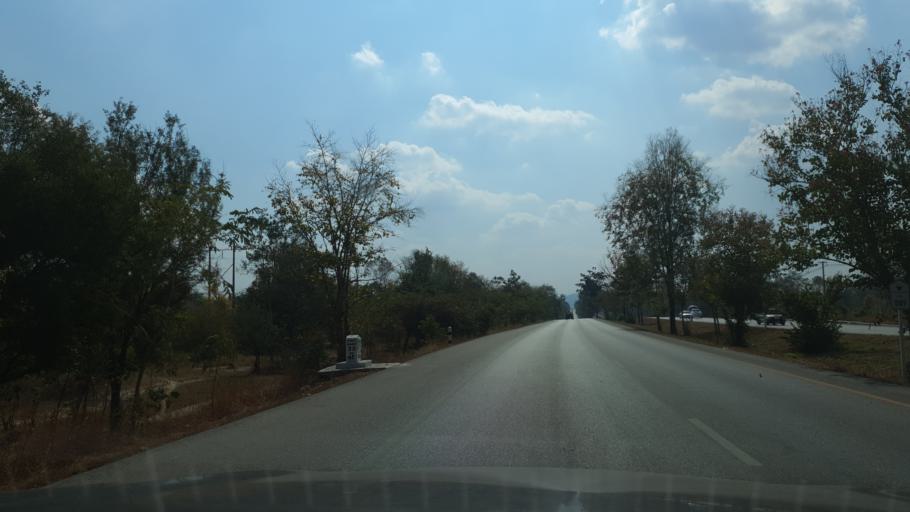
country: TH
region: Lampang
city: Mae Phrik
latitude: 17.3992
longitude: 99.1497
